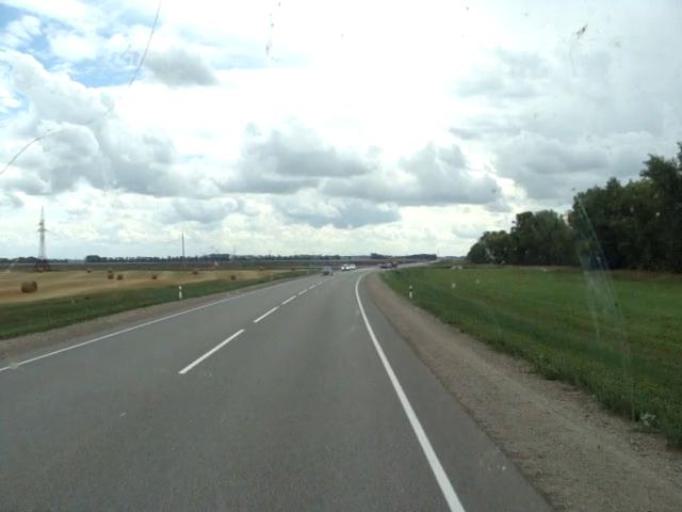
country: RU
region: Altai Krai
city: Shubenka
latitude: 52.6791
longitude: 85.0493
